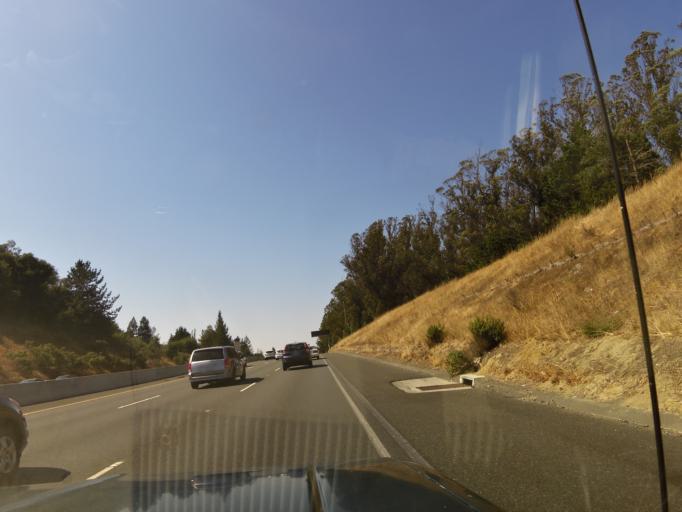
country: US
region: California
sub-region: Sonoma County
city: Cotati
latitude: 38.3070
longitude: -122.7105
